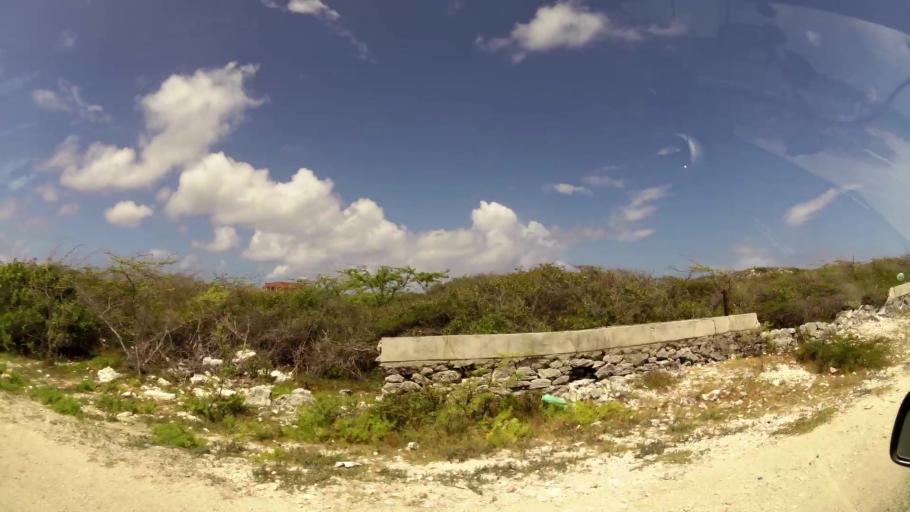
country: TC
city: Cockburn Town
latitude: 21.4874
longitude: -71.1420
